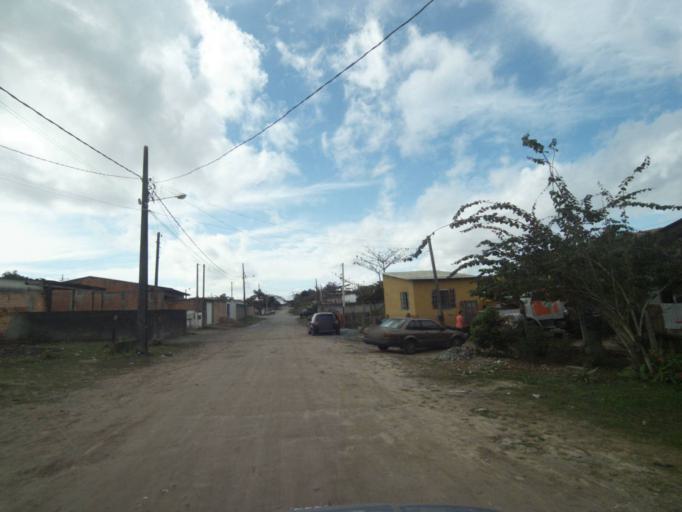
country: BR
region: Parana
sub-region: Paranagua
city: Paranagua
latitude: -25.5706
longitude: -48.5658
